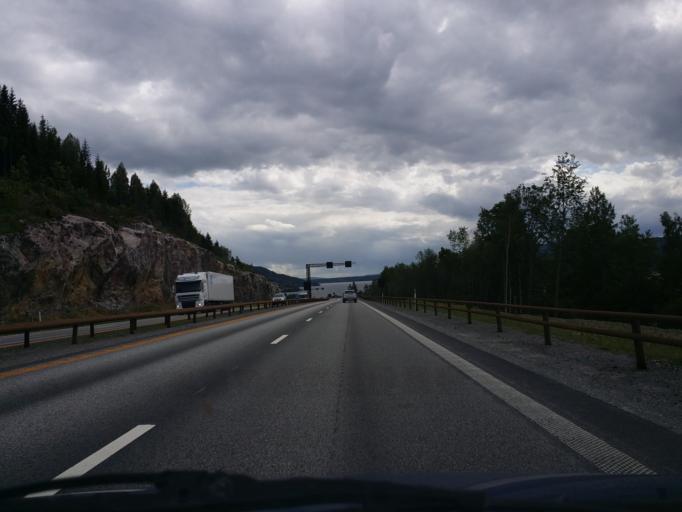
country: NO
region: Akershus
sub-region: Eidsvoll
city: Eidsvoll
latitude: 60.4908
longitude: 11.2362
